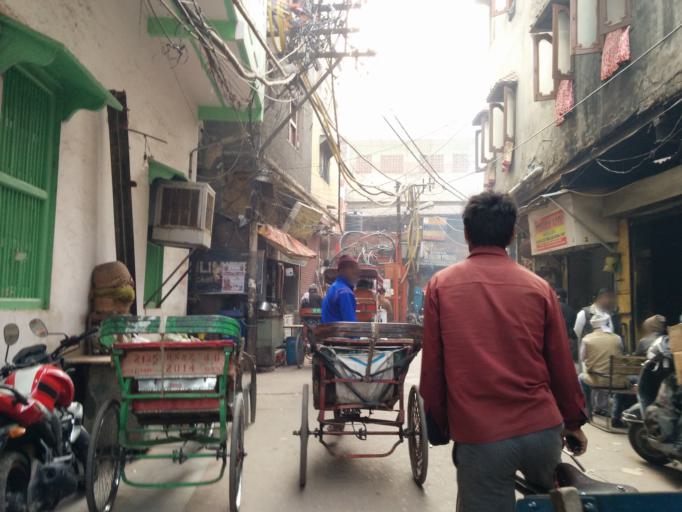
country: IN
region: NCT
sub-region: North Delhi
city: Delhi
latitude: 28.6486
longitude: 77.2305
